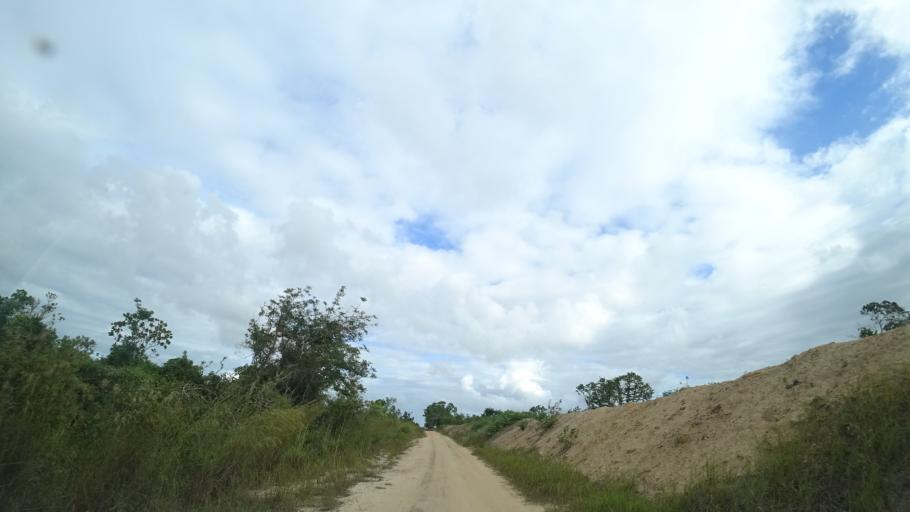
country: MZ
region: Sofala
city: Beira
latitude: -19.6182
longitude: 35.0605
